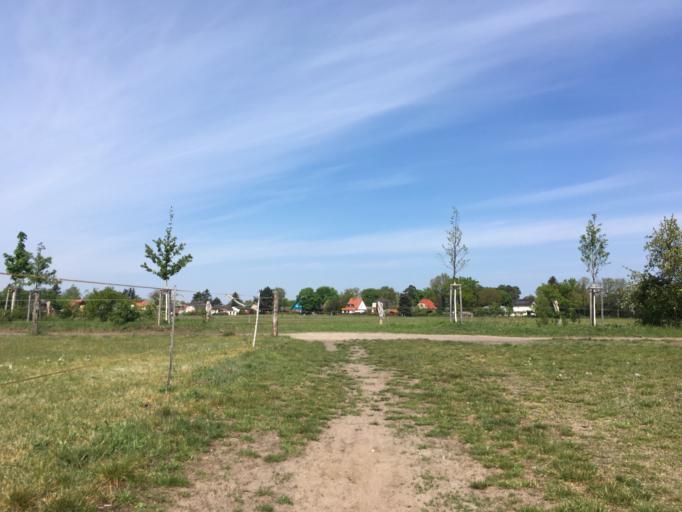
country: DE
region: Berlin
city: Blankenfelde
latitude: 52.6402
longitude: 13.3807
